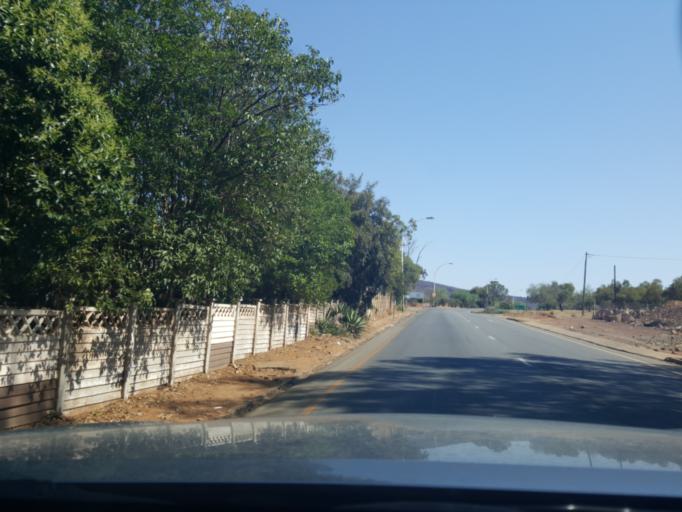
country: ZA
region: North-West
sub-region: Ngaka Modiri Molema District Municipality
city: Zeerust
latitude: -25.5402
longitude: 26.0777
